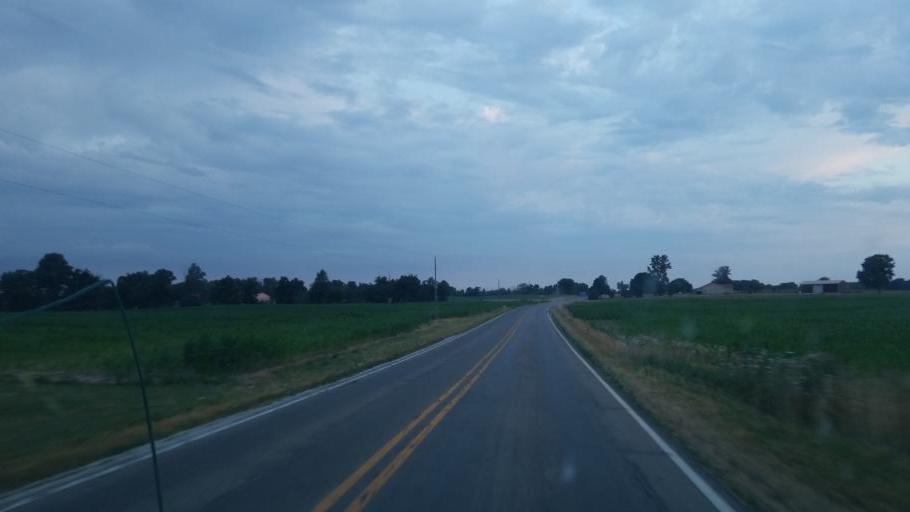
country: US
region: Ohio
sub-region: Defiance County
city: Hicksville
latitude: 41.3261
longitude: -84.8056
